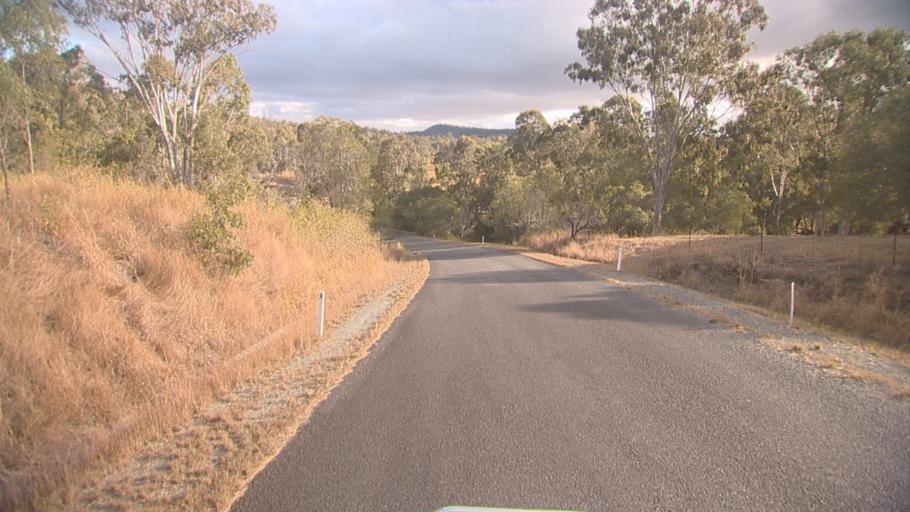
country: AU
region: Queensland
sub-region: Logan
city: Cedar Vale
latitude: -27.9039
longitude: 153.0648
